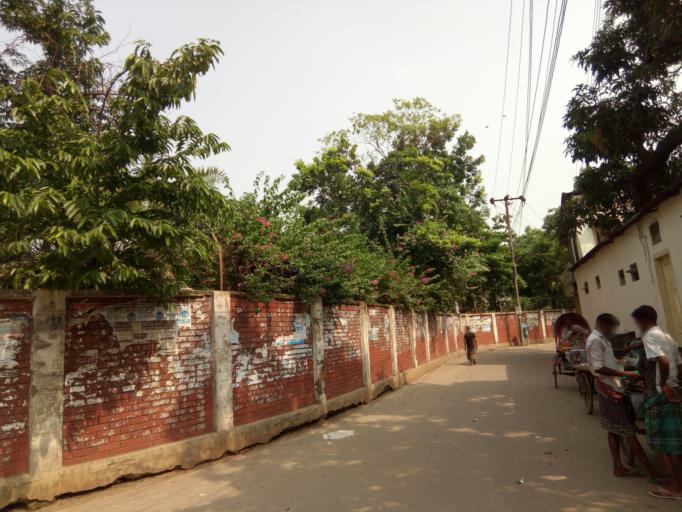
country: BD
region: Dhaka
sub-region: Dhaka
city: Dhaka
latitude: 23.6960
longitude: 90.4277
